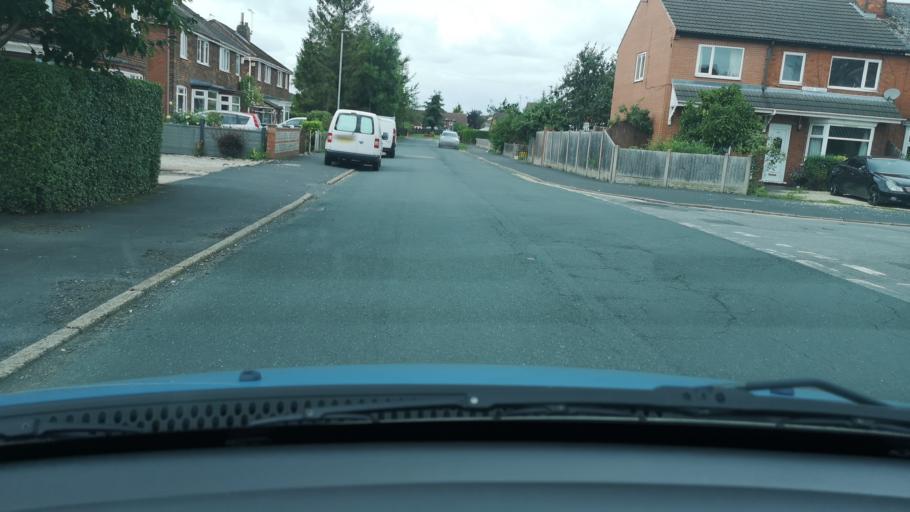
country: GB
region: England
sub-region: North Lincolnshire
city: Scunthorpe
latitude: 53.5862
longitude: -0.6863
